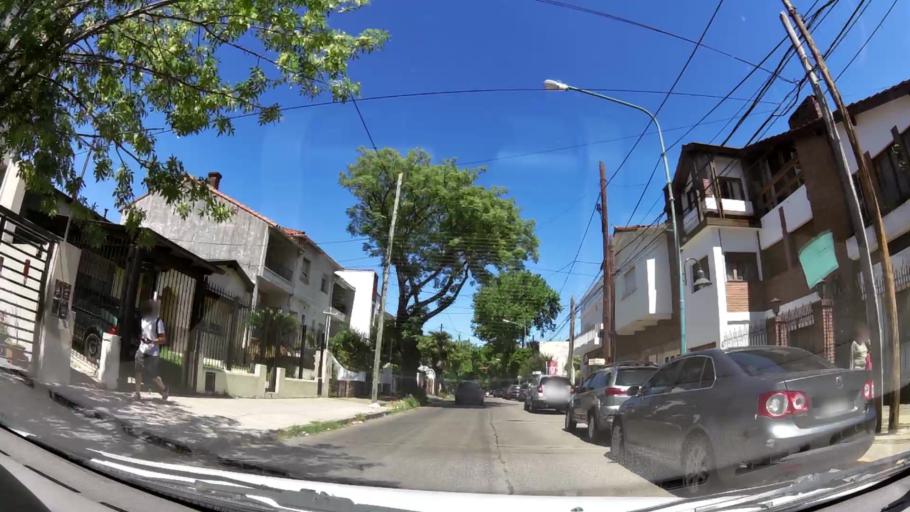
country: AR
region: Buenos Aires
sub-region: Partido de Vicente Lopez
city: Olivos
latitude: -34.5086
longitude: -58.4929
